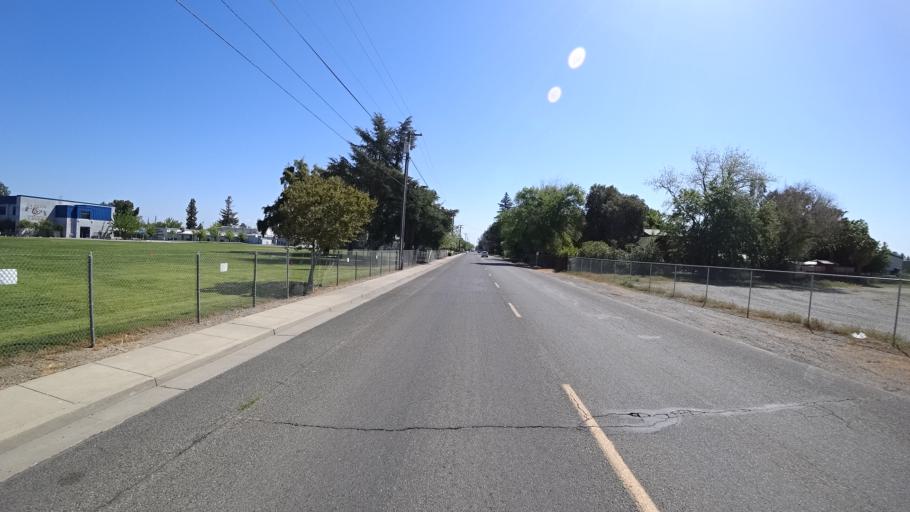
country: US
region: California
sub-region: Glenn County
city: Orland
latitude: 39.7402
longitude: -122.1944
